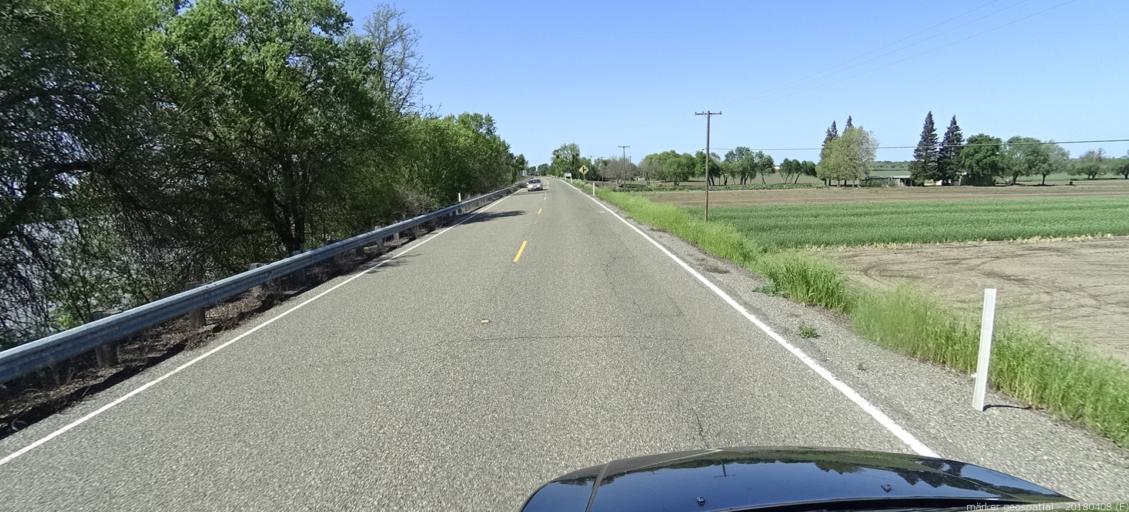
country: US
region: California
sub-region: Sacramento County
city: Laguna
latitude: 38.4080
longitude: -121.5154
